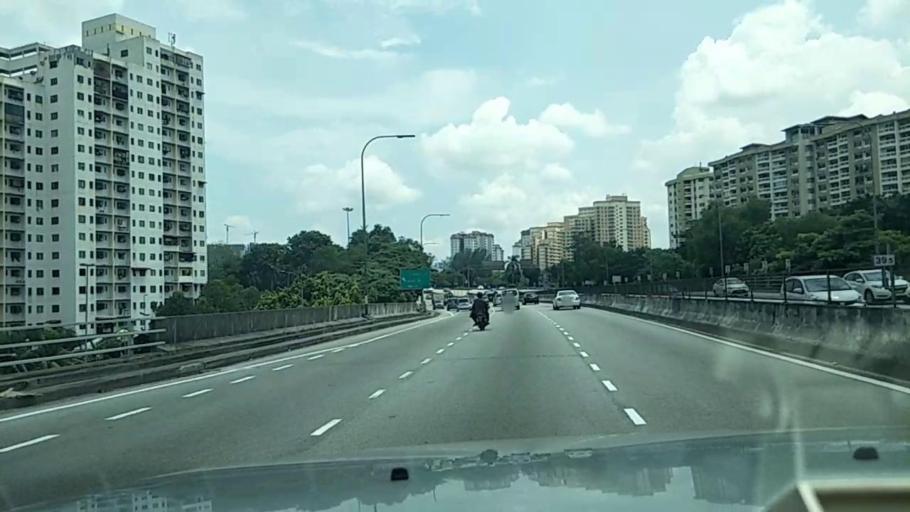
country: MY
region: Selangor
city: Kampong Baharu Balakong
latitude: 3.0663
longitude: 101.7071
